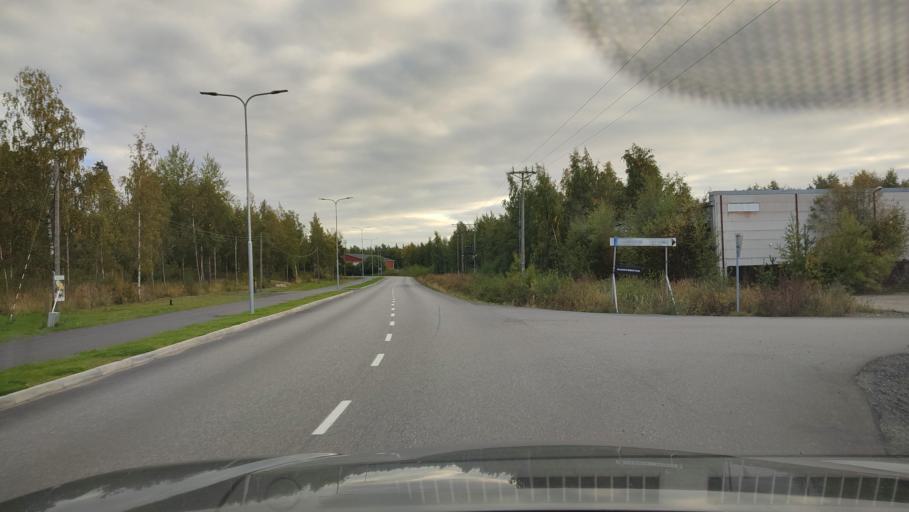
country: FI
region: Ostrobothnia
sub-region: Sydosterbotten
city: Kristinestad
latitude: 62.2647
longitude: 21.3838
